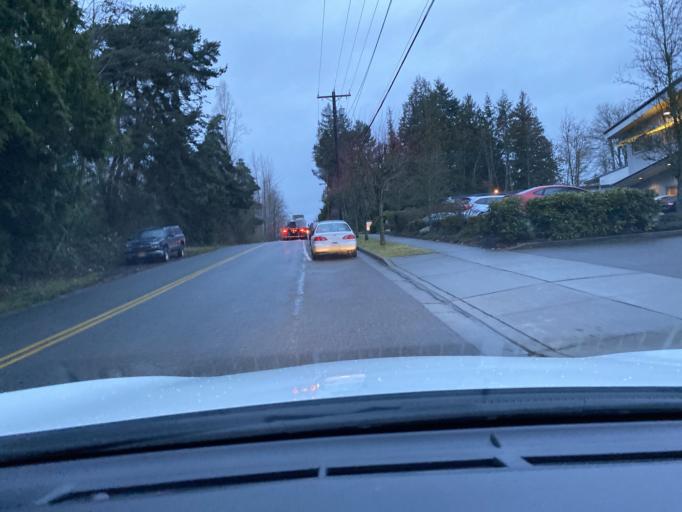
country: US
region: Washington
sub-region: Snohomish County
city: Mukilteo
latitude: 47.8911
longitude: -122.2897
